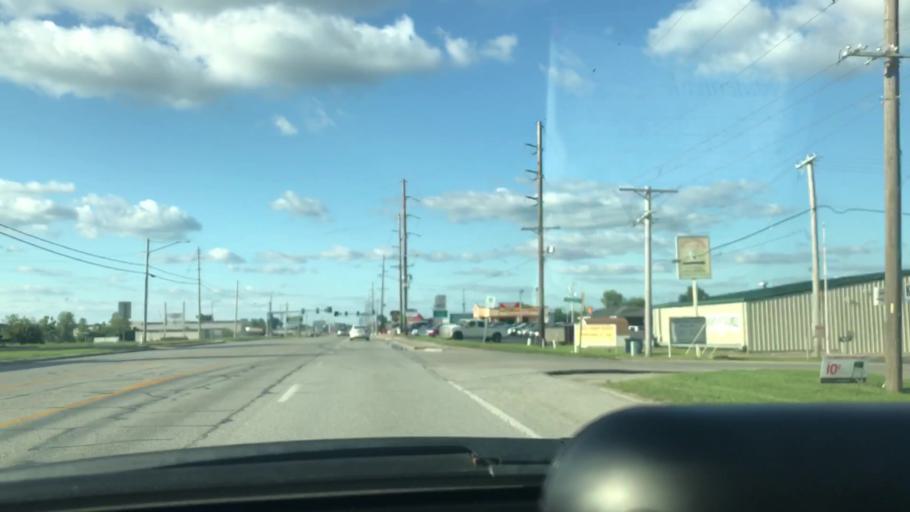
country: US
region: Missouri
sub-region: Pettis County
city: Sedalia
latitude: 38.6723
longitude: -93.2517
